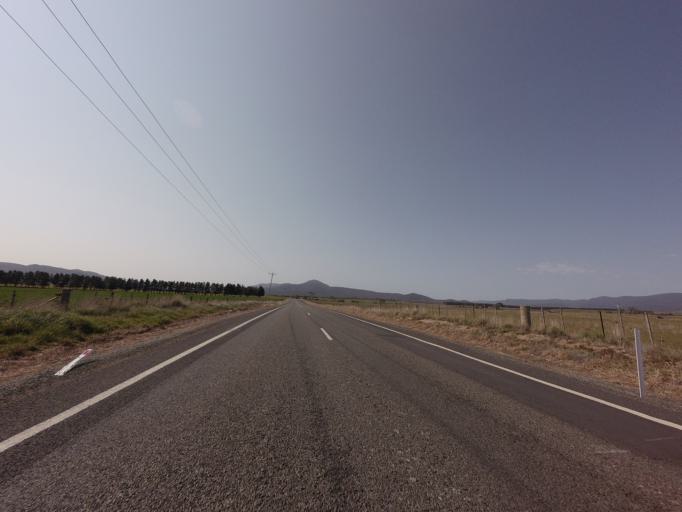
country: AU
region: Tasmania
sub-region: Northern Midlands
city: Evandale
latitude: -41.8010
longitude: 147.6919
